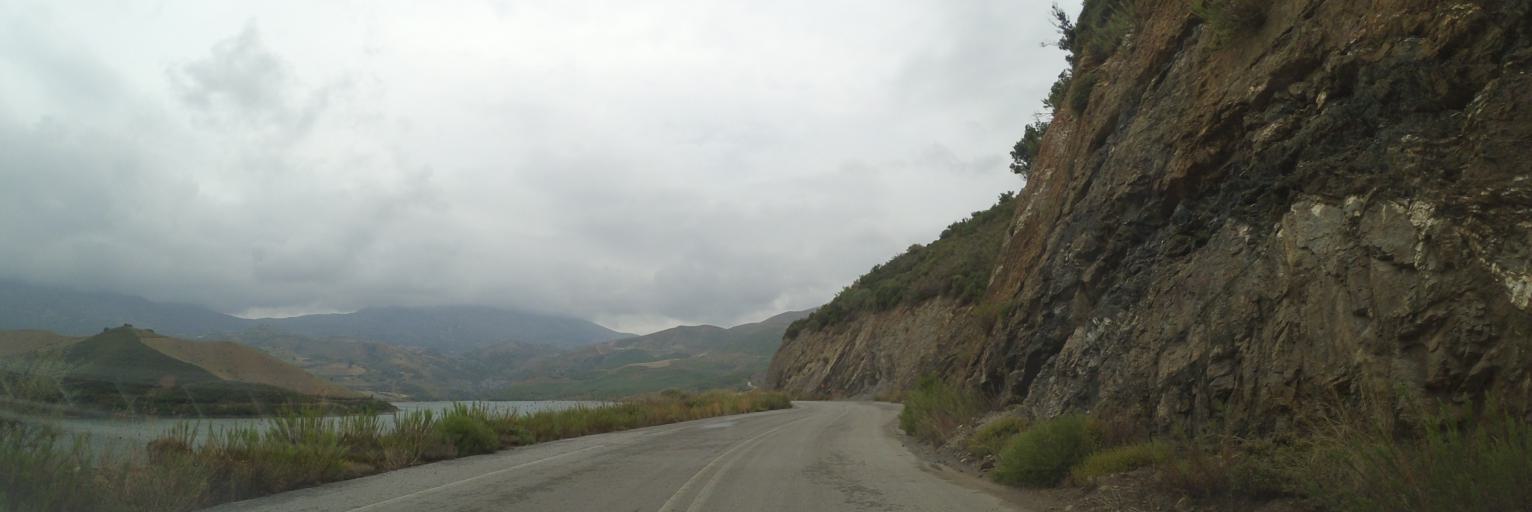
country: GR
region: Crete
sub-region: Nomos Rethymnis
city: Agia Foteini
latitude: 35.2846
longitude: 24.5729
